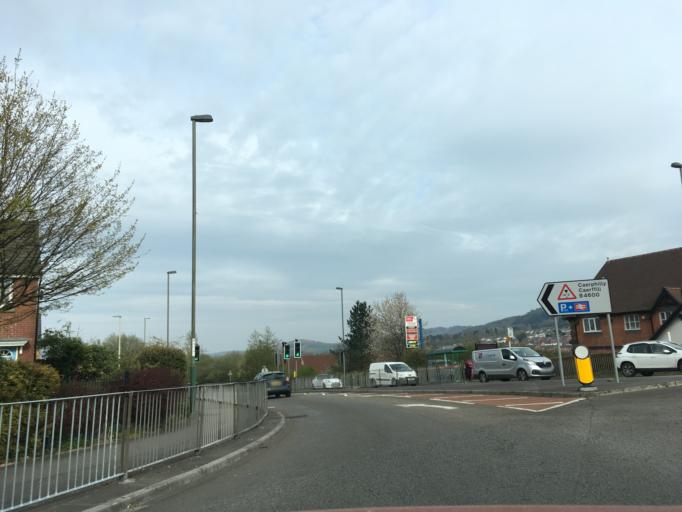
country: GB
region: Wales
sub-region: Caerphilly County Borough
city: Caerphilly
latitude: 51.5712
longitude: -3.2430
